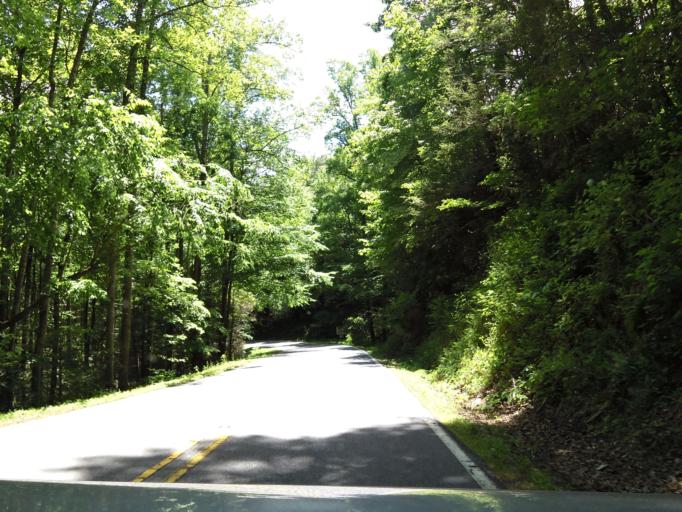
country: US
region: North Carolina
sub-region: Graham County
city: Robbinsville
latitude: 35.4695
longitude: -83.9218
